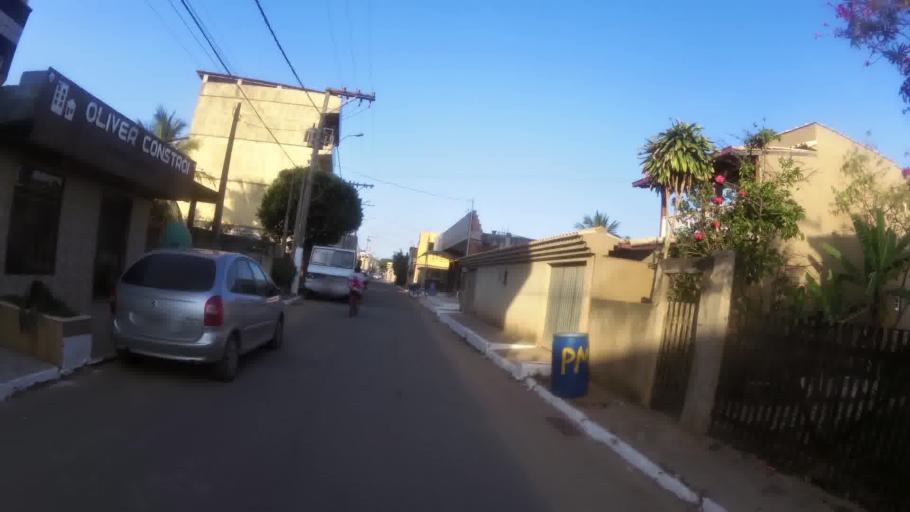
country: BR
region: Espirito Santo
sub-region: Piuma
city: Piuma
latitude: -20.8899
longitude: -40.7795
